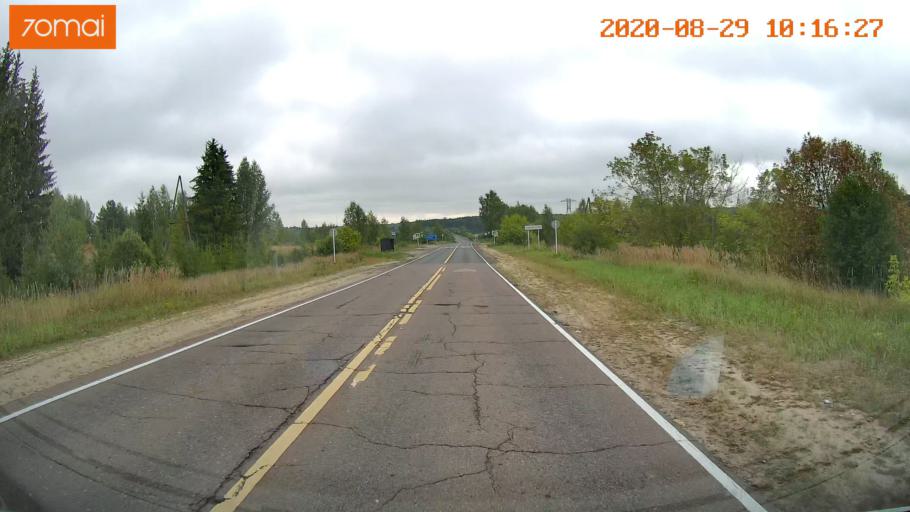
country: RU
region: Ivanovo
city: Yur'yevets
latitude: 57.3381
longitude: 42.7925
